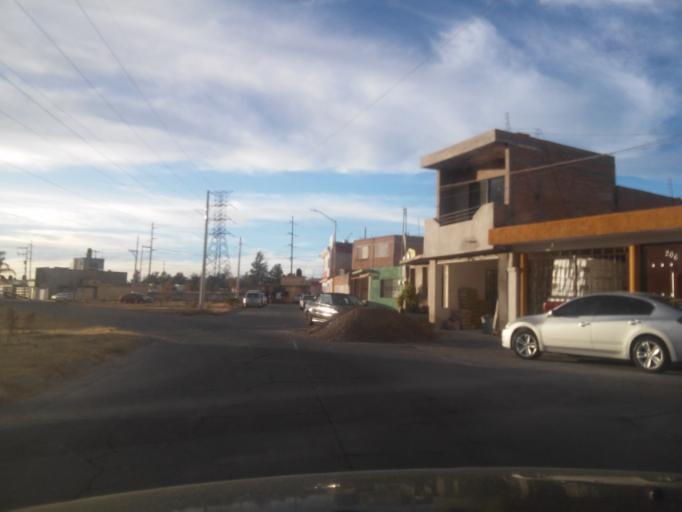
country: MX
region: Durango
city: Victoria de Durango
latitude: 24.0039
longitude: -104.6330
